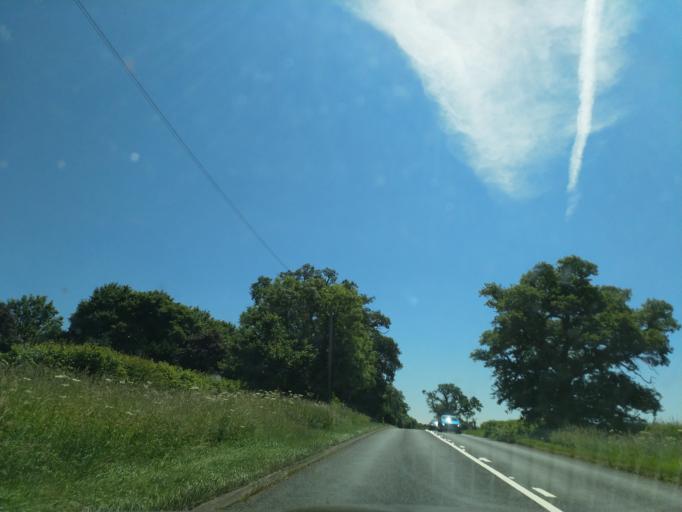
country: GB
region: England
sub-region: Warwickshire
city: Warwick
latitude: 52.2451
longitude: -1.5563
